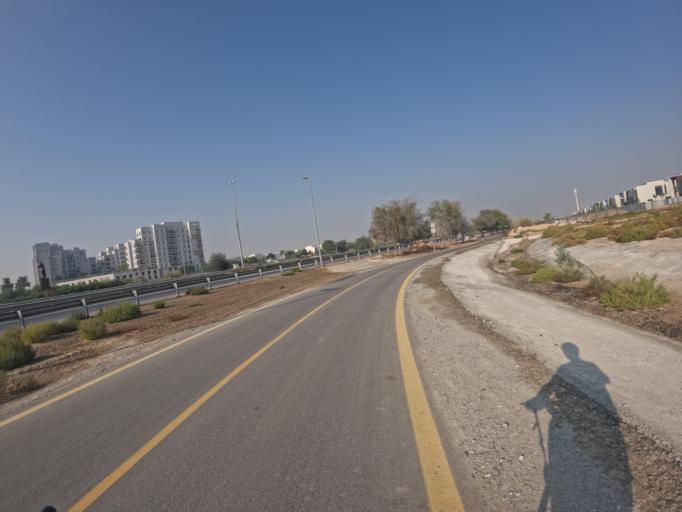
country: AE
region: Dubai
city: Dubai
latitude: 25.0130
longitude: 55.2912
